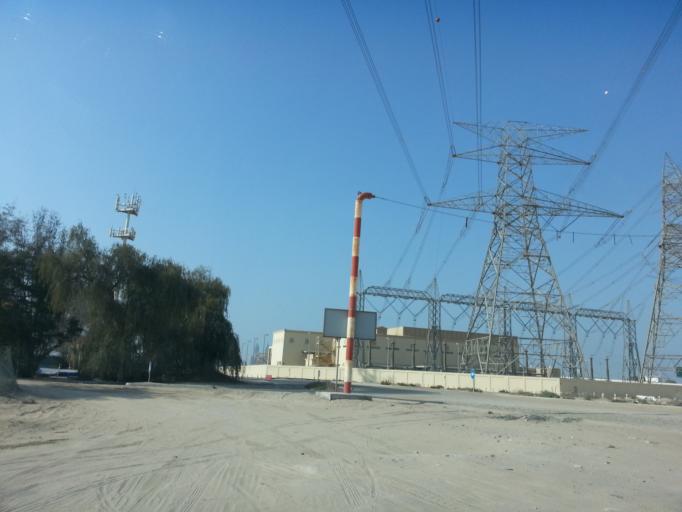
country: AE
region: Dubai
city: Dubai
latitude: 25.0643
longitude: 55.1945
